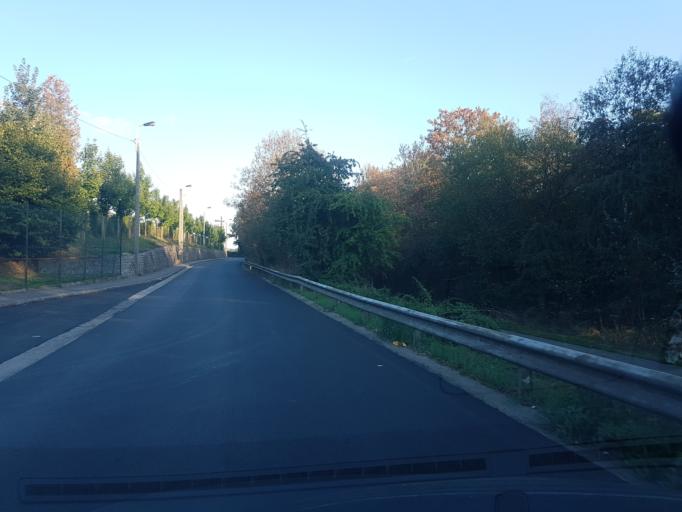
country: BE
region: Wallonia
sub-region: Province de Liege
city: Chaudfontaine
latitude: 50.6170
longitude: 5.6227
